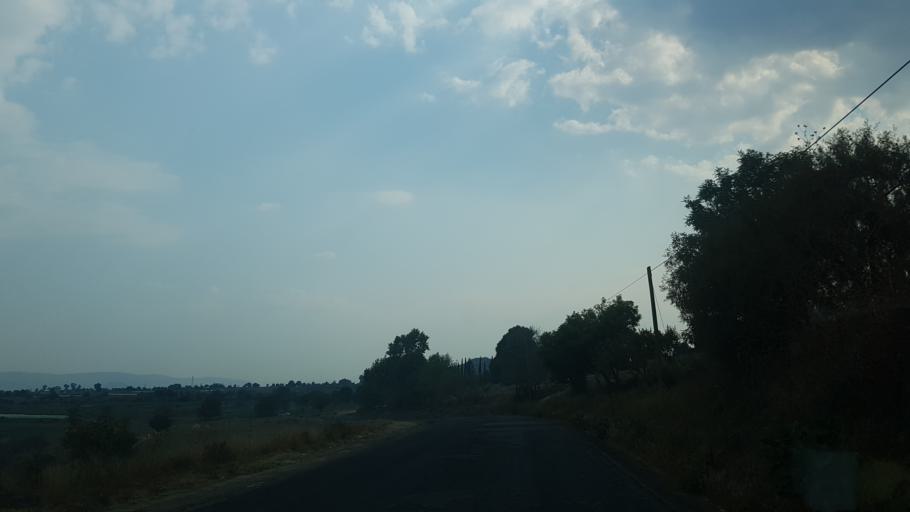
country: MX
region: Puebla
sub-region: Santa Isabel Cholula
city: San Martin Tlamapa
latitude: 18.9684
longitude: -98.3954
